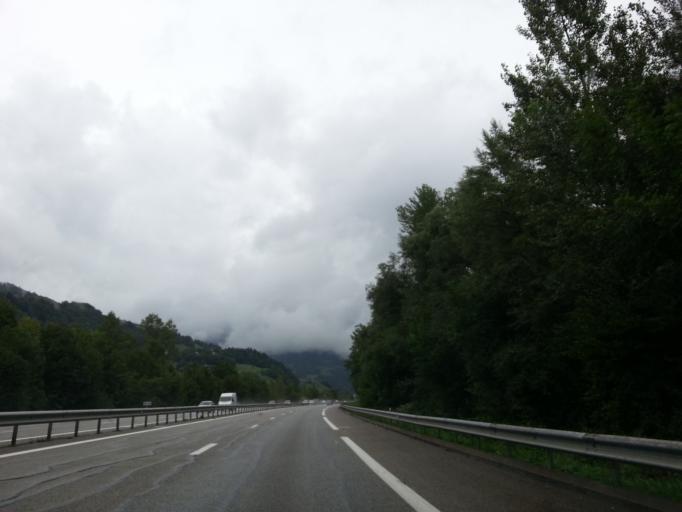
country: FR
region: Rhone-Alpes
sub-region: Departement de la Savoie
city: Marthod
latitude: 45.7194
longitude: 6.4100
